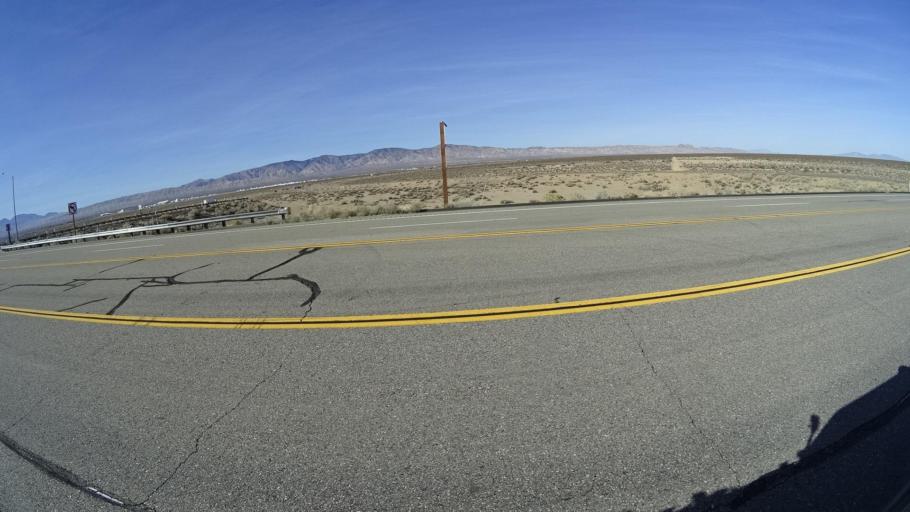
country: US
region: California
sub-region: Kern County
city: Mojave
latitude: 35.0387
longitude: -118.1049
